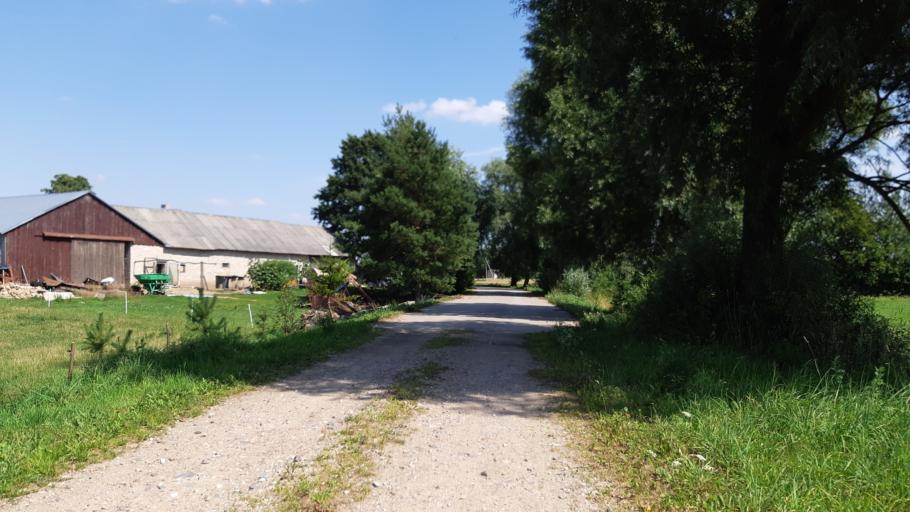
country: LT
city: Virbalis
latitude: 54.6192
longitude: 22.8145
